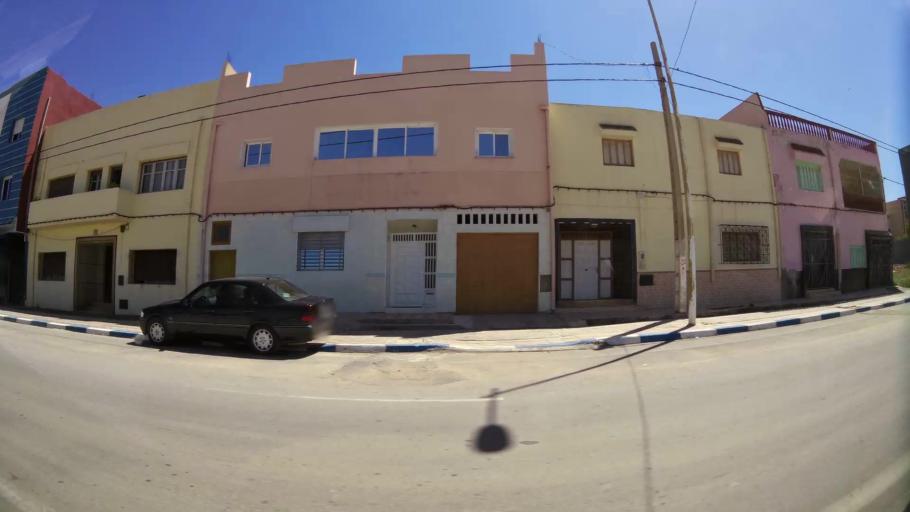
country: MA
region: Oriental
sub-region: Berkane-Taourirt
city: Madagh
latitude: 35.1368
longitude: -2.4157
